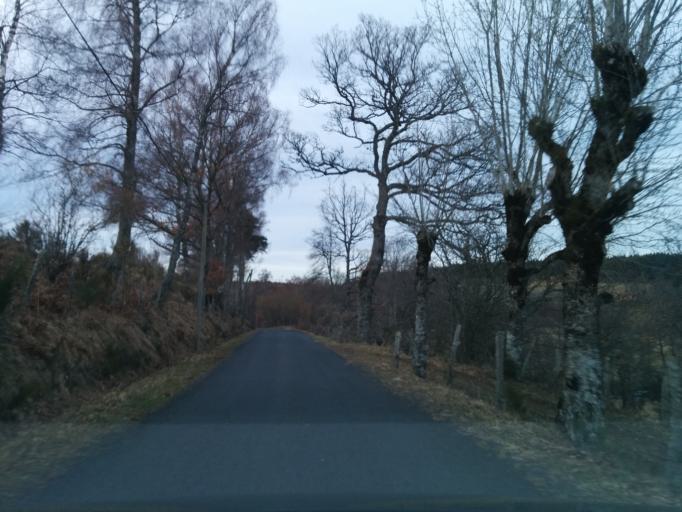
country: FR
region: Auvergne
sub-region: Departement du Cantal
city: Chaudes-Aigues
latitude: 44.8197
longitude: 2.8941
